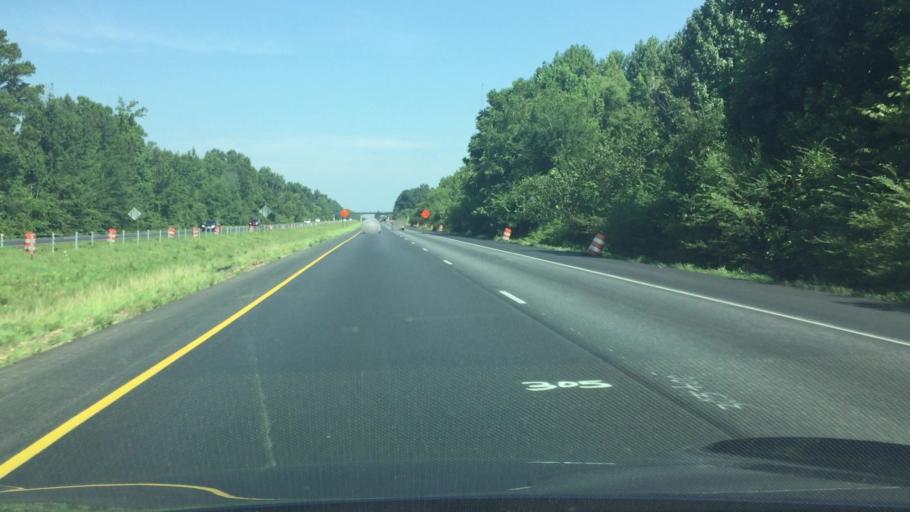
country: US
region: Alabama
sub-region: Autauga County
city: Marbury
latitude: 32.7563
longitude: -86.5562
